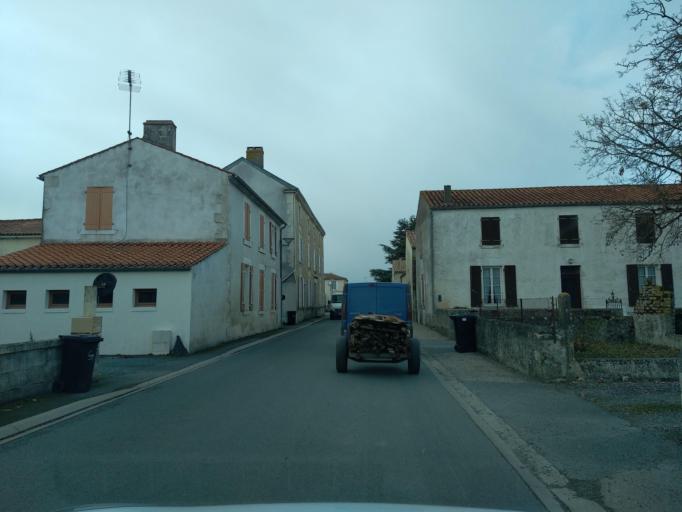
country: FR
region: Pays de la Loire
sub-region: Departement de la Vendee
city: Vix
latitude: 46.3621
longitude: -0.8564
